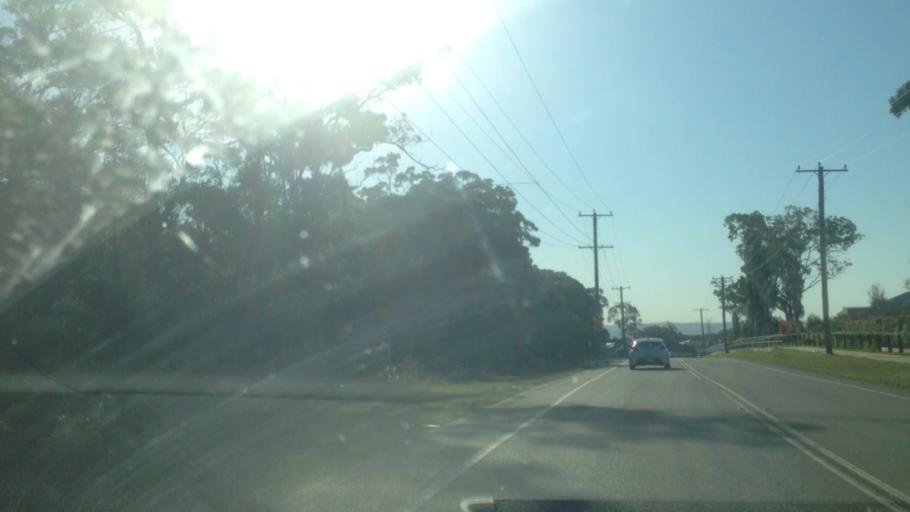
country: AU
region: New South Wales
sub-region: Lake Macquarie Shire
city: Dora Creek
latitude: -33.1119
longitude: 151.5098
